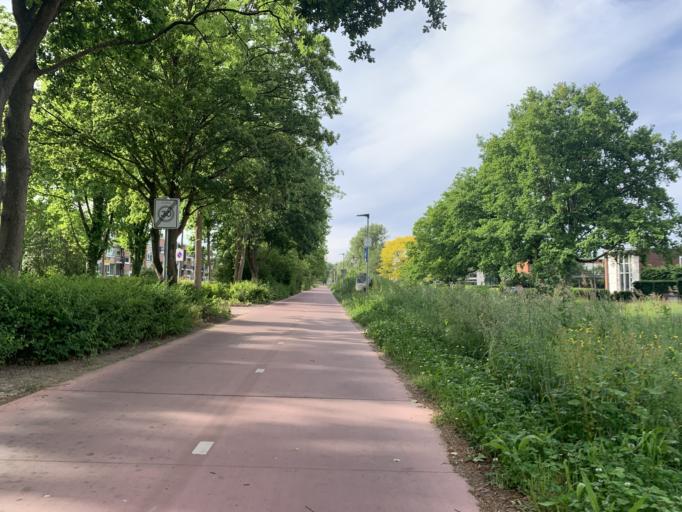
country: NL
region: Groningen
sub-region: Gemeente Haren
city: Haren
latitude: 53.1927
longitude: 6.5957
